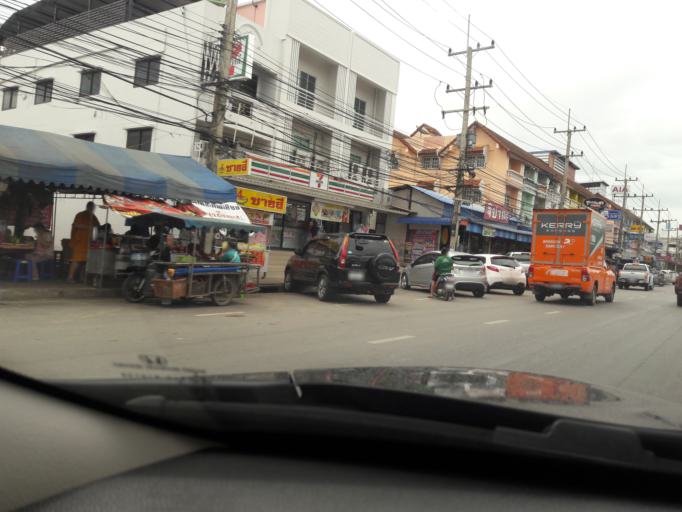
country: TH
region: Ratchaburi
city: Damnoen Saduak
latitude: 13.5352
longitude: 99.9656
